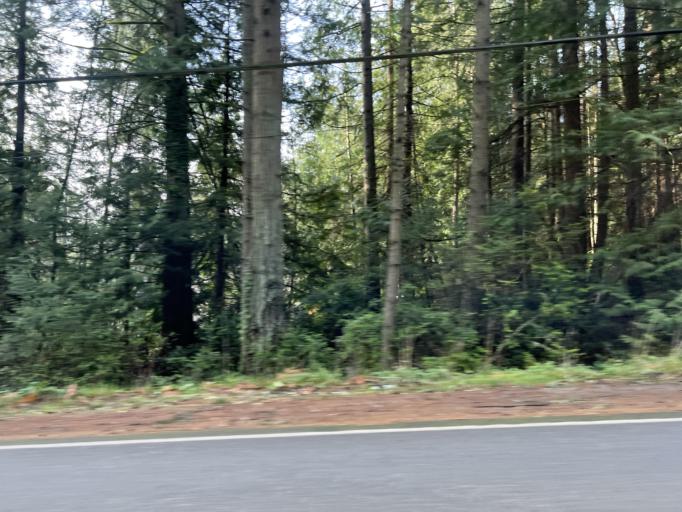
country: US
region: Washington
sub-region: Kitsap County
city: Bainbridge Island
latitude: 47.6594
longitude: -122.5191
